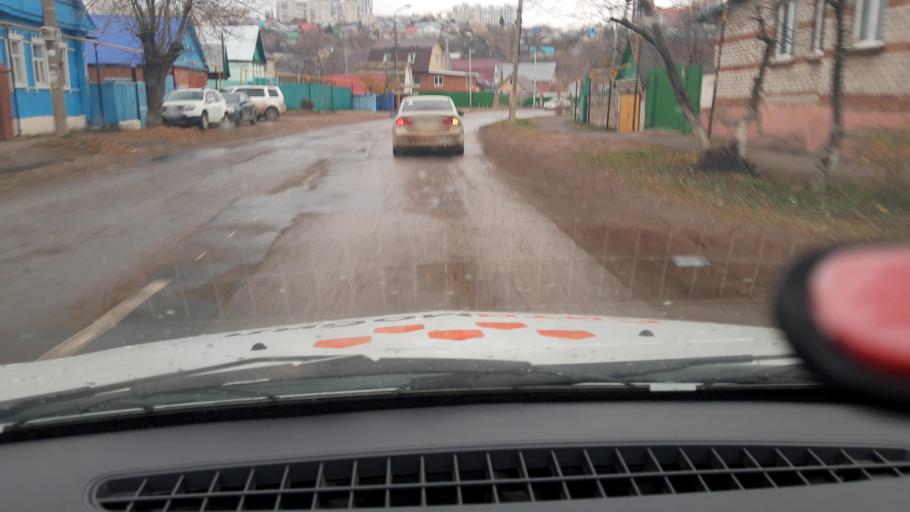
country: RU
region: Bashkortostan
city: Ufa
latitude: 54.7394
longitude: 55.9206
